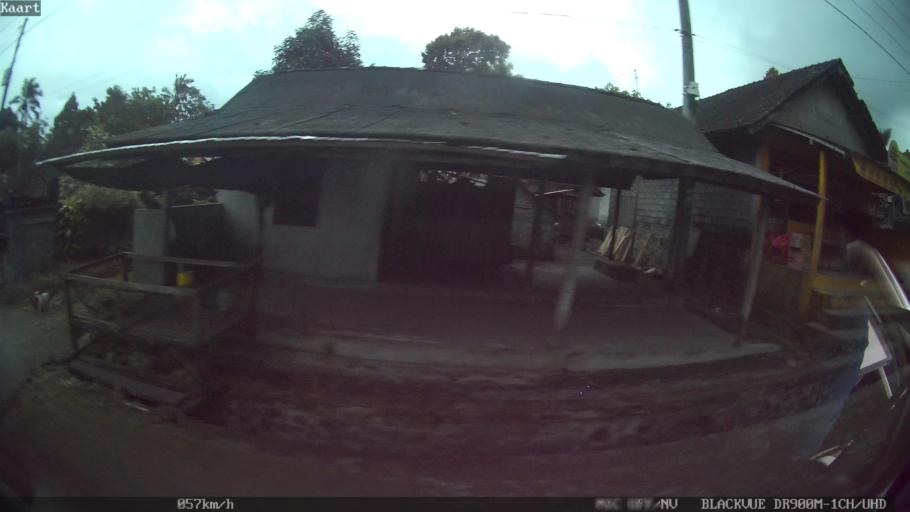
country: ID
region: Bali
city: Banjar Tiga
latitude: -8.3784
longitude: 115.4180
